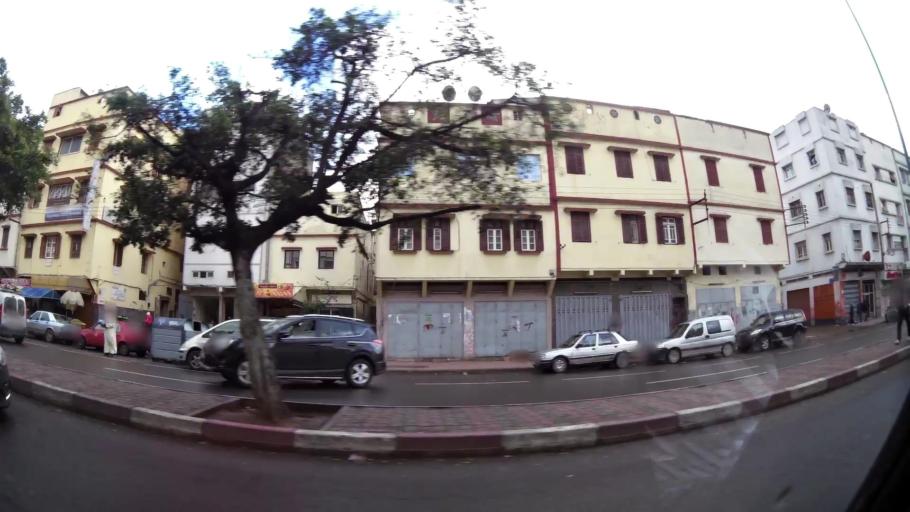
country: MA
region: Grand Casablanca
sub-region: Casablanca
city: Casablanca
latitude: 33.5480
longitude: -7.5740
